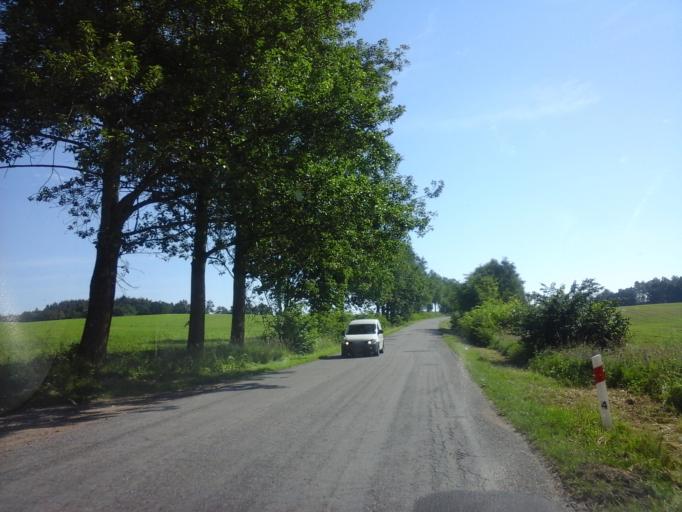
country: PL
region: West Pomeranian Voivodeship
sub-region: Powiat swidwinski
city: Polczyn-Zdroj
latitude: 53.6856
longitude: 16.0235
